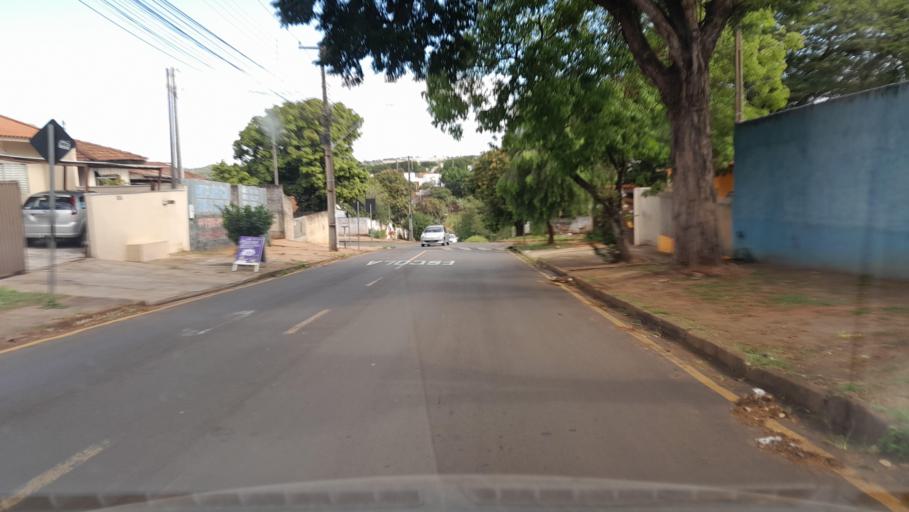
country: BR
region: Parana
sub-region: Umuarama
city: Umuarama
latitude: -23.7715
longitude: -53.3028
